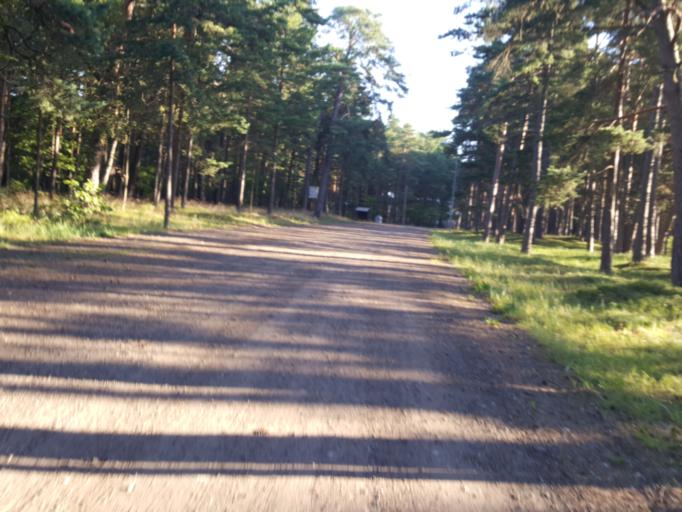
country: LV
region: Salacgrivas
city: Ainazi
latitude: 57.8590
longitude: 24.3513
